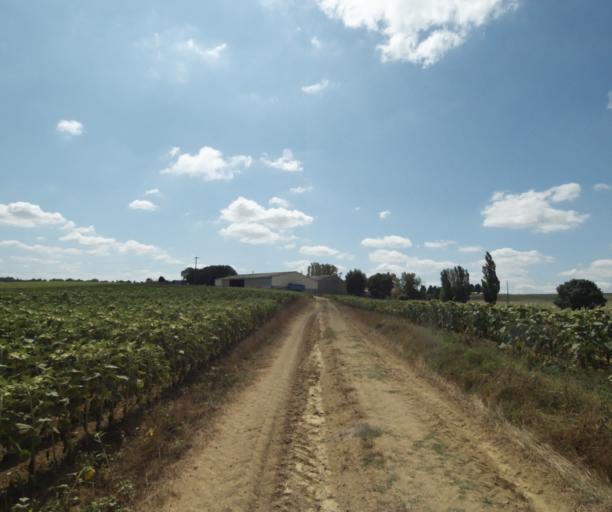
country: FR
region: Midi-Pyrenees
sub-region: Departement de la Haute-Garonne
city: Auriac-sur-Vendinelle
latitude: 43.4690
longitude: 1.8238
